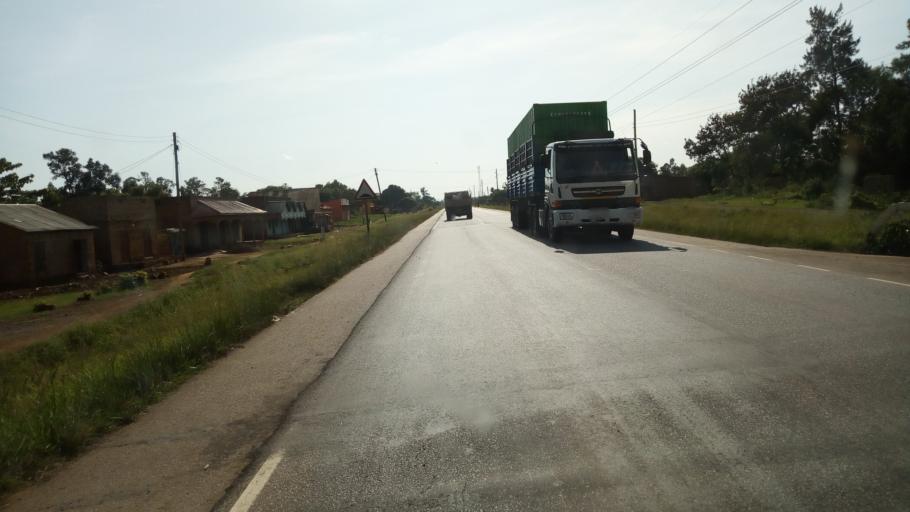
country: UG
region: Eastern Region
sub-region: Bugiri District
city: Bugiri
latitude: 0.5318
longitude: 33.8731
